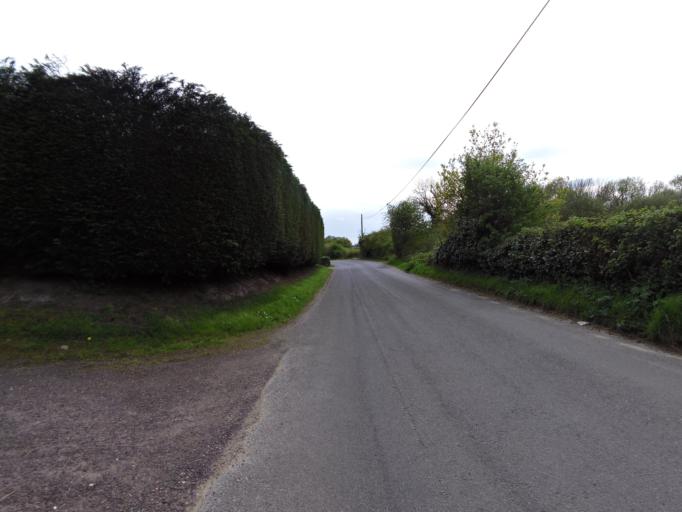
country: GB
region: England
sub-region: Suffolk
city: Ipswich
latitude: 51.9726
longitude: 1.1684
